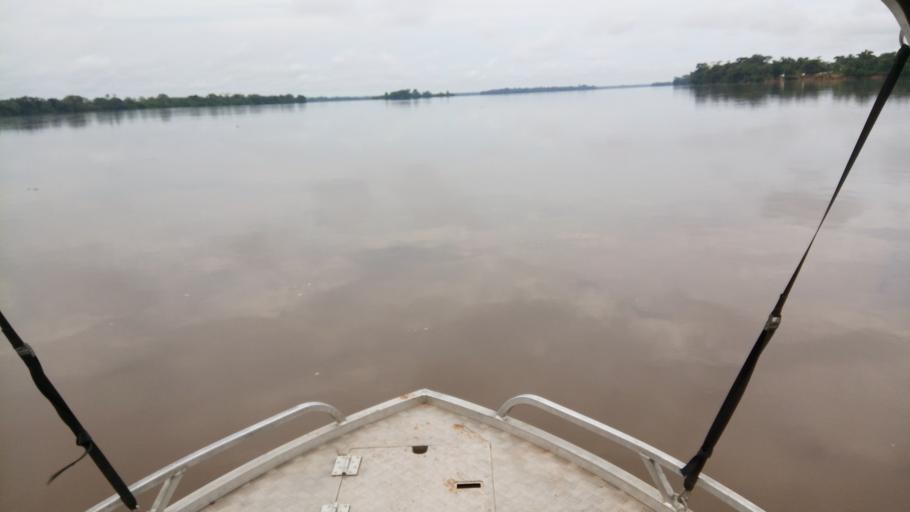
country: CD
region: Eastern Province
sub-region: Sous-Region de la Tshopo
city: Yangambi
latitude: 0.7576
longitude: 24.3365
